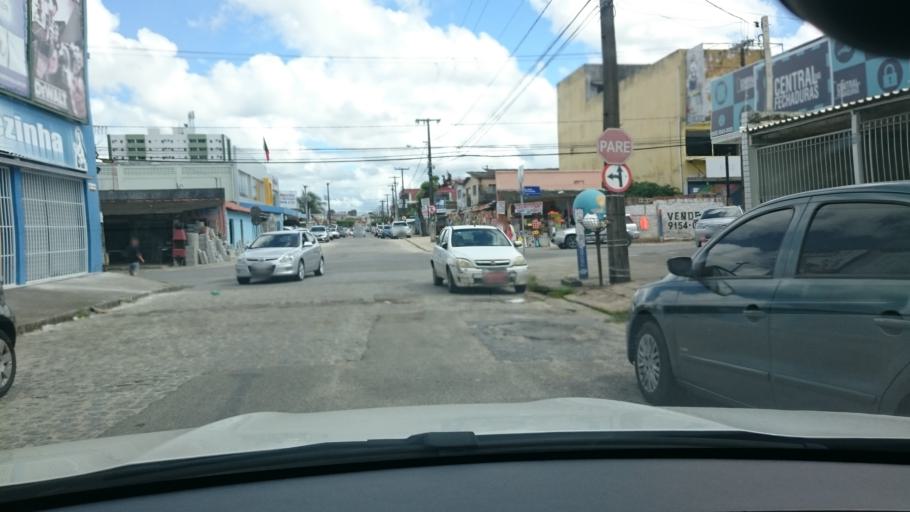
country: BR
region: Paraiba
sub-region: Joao Pessoa
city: Joao Pessoa
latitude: -7.1234
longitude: -34.8627
